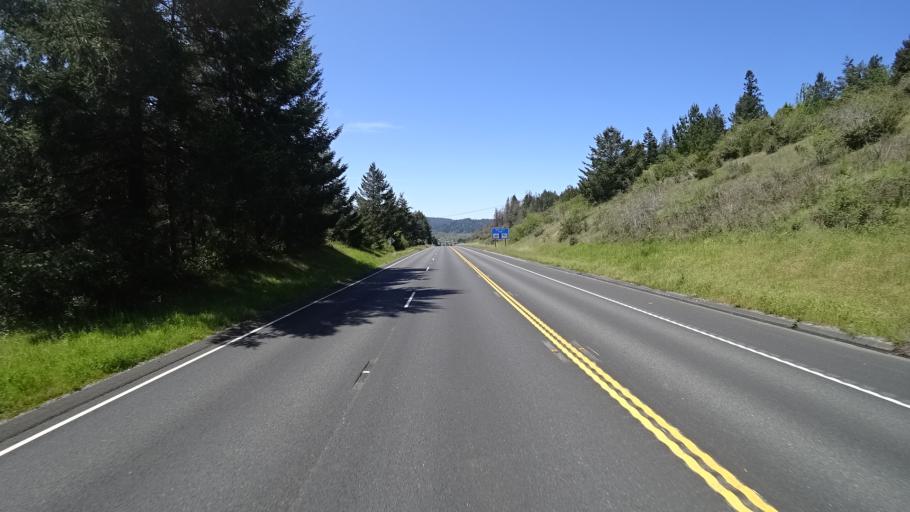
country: US
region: California
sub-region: Humboldt County
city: Blue Lake
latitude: 40.8875
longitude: -123.9844
